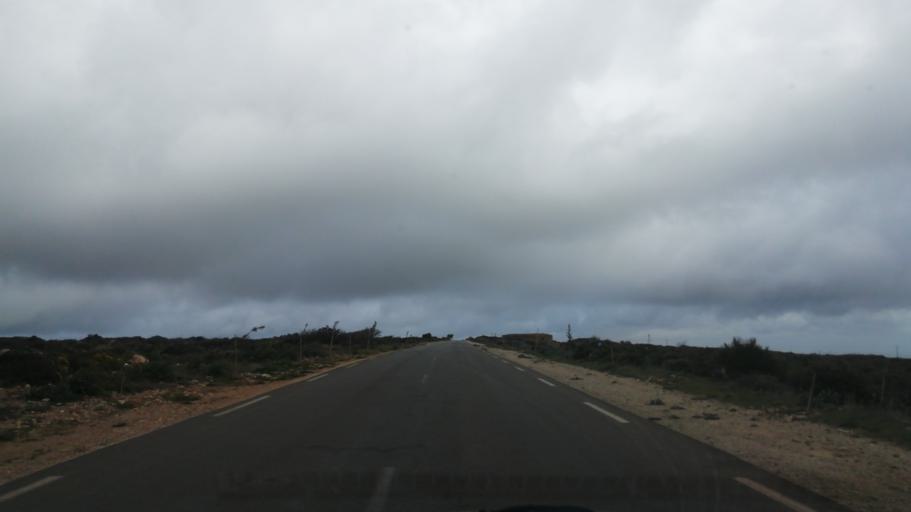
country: DZ
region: Oran
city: Mers el Kebir
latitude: 35.7051
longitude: -0.7363
